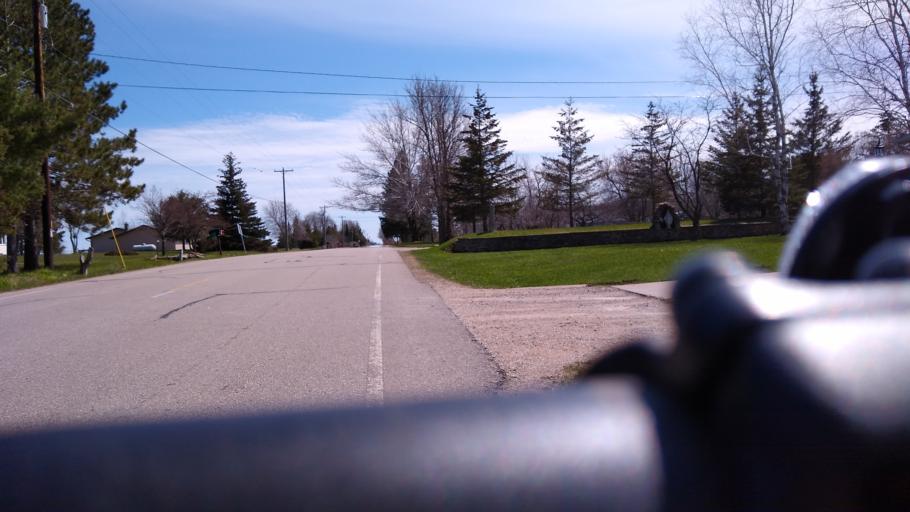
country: US
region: Michigan
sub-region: Delta County
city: Escanaba
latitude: 45.7221
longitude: -87.2025
